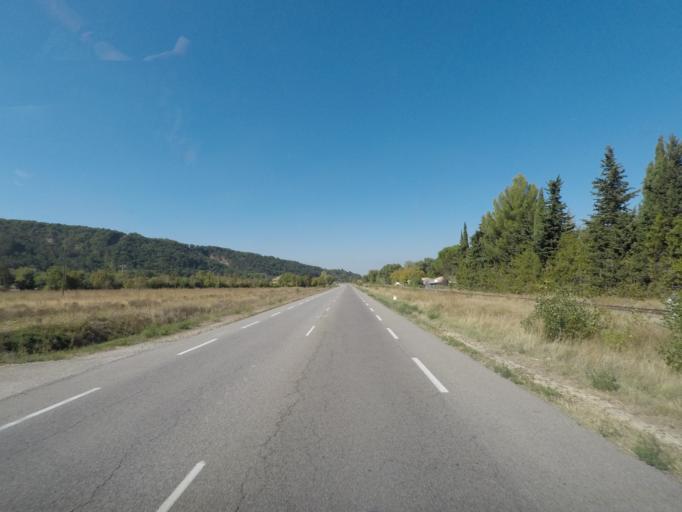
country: FR
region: Rhone-Alpes
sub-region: Departement de la Drome
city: Aouste-sur-Sye
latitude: 44.7134
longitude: 5.0495
